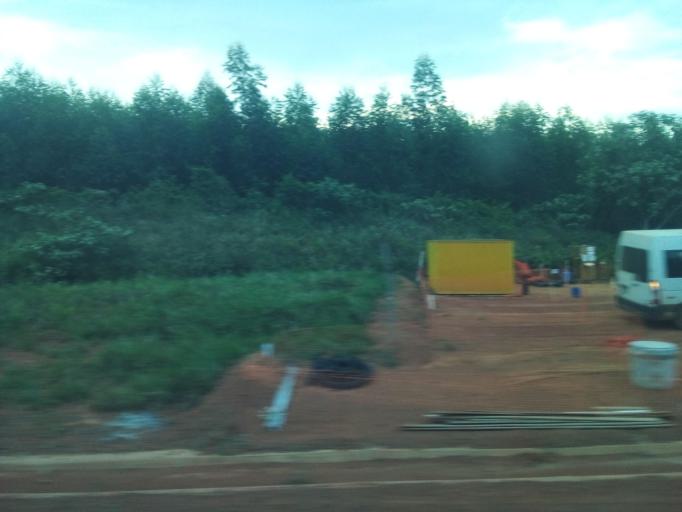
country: BR
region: Maranhao
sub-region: Imperatriz
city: Imperatriz
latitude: -4.7305
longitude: -47.3080
